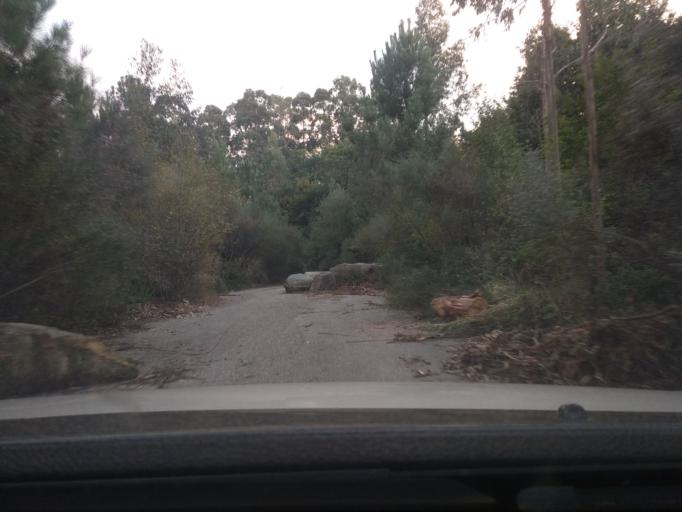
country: ES
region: Galicia
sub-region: Provincia de Pontevedra
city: Moana
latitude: 42.3018
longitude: -8.6960
